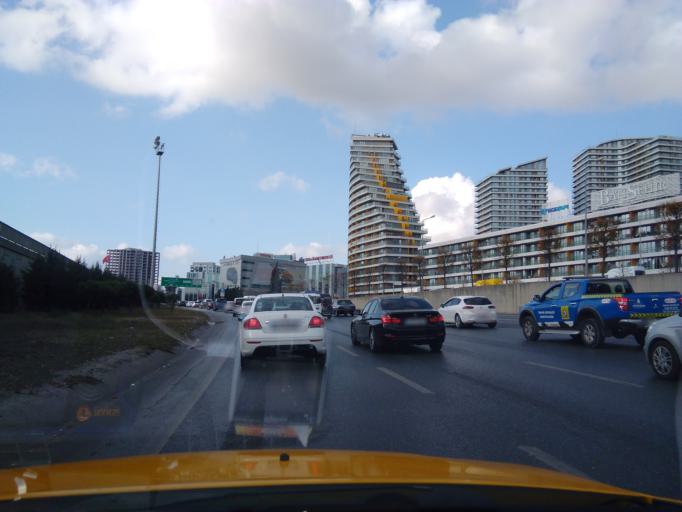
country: TR
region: Istanbul
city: Mahmutbey
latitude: 41.0625
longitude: 28.8403
